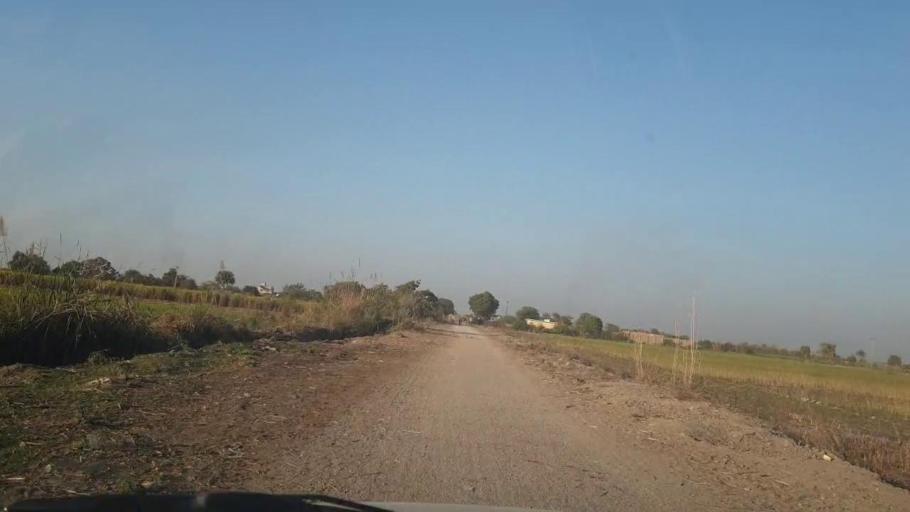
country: PK
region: Sindh
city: Mirpur Khas
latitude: 25.4676
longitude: 69.0855
